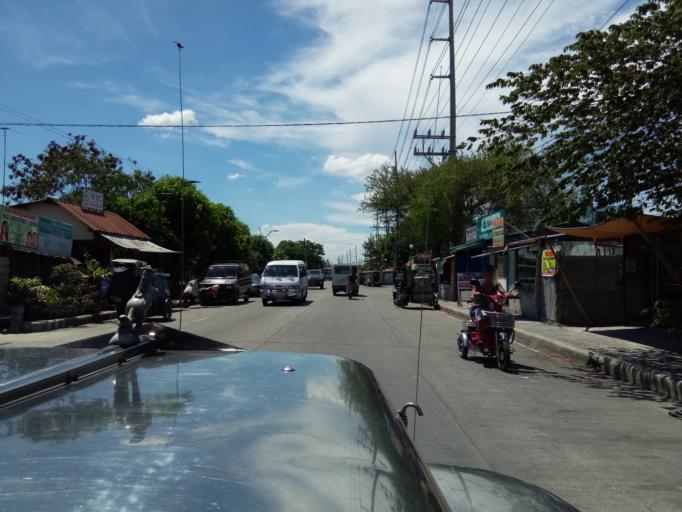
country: PH
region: Calabarzon
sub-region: Province of Cavite
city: General Trias
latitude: 14.3705
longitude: 120.8892
